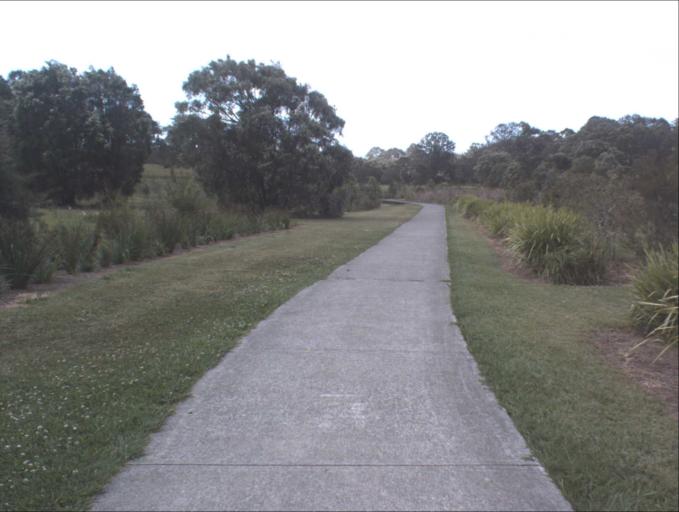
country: AU
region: Queensland
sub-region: Logan
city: Slacks Creek
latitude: -27.6705
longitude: 153.1578
